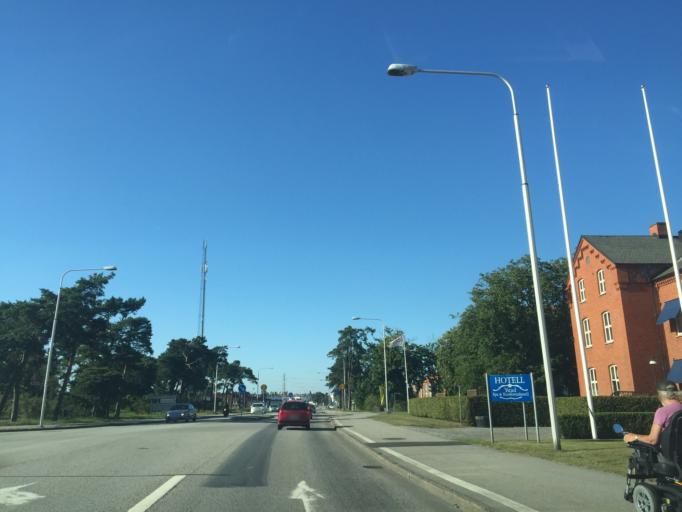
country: SE
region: Skane
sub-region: Ystads Kommun
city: Ystad
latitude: 55.4318
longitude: 13.8395
